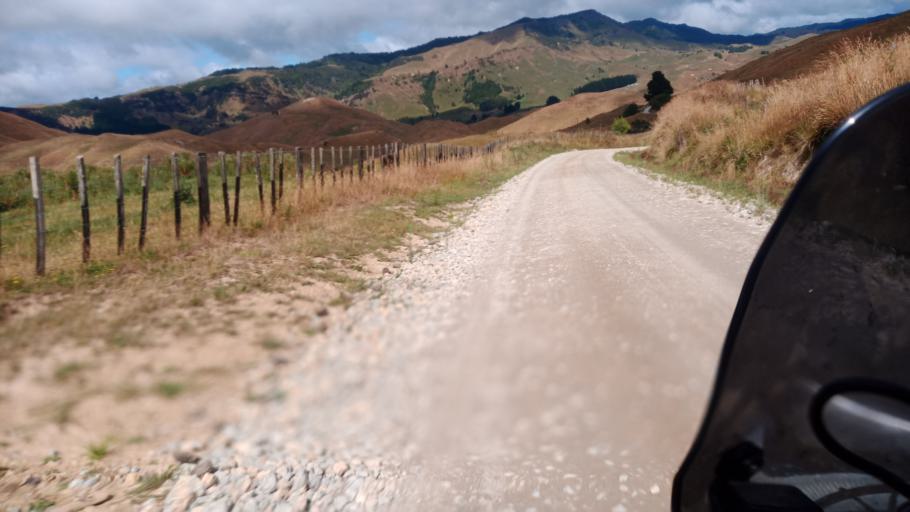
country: NZ
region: Hawke's Bay
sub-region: Wairoa District
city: Wairoa
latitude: -38.6102
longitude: 177.4446
